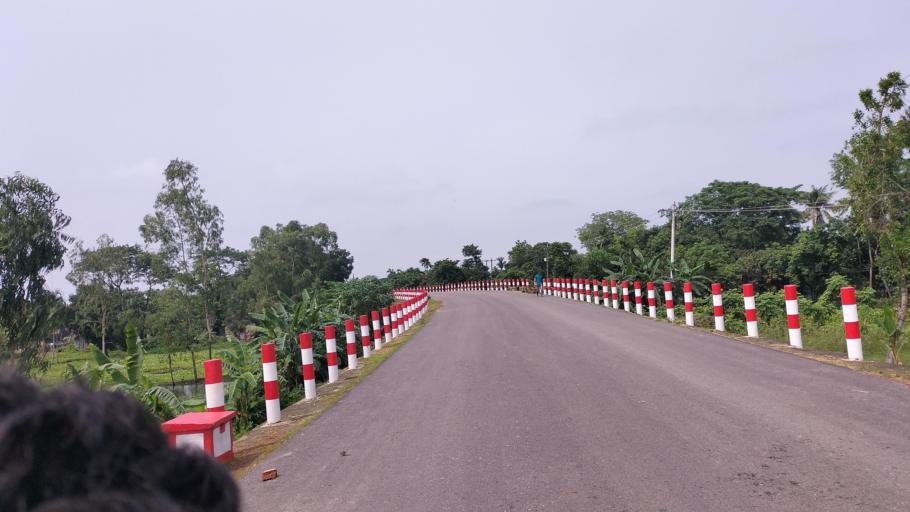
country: BD
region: Dhaka
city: Netrakona
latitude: 24.9523
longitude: 90.8335
